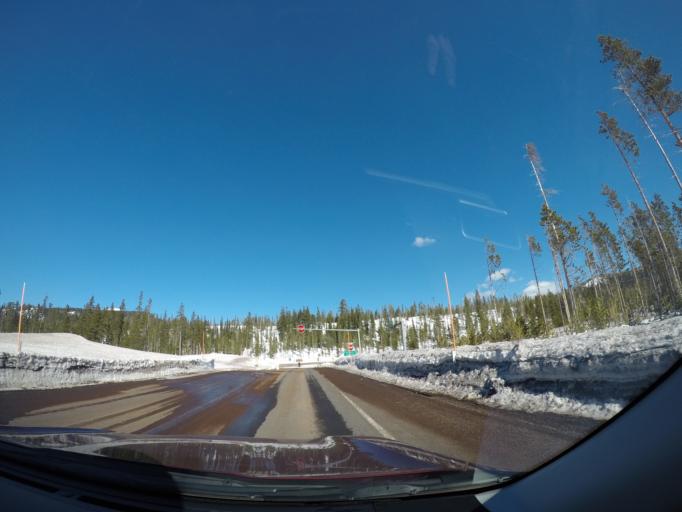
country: US
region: Oregon
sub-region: Deschutes County
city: Sunriver
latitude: 43.9815
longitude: -121.6134
